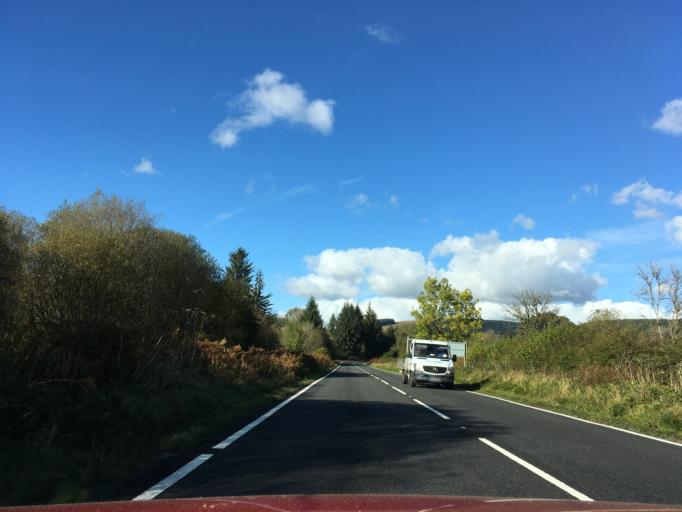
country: GB
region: Wales
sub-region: Merthyr Tydfil County Borough
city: Merthyr Tydfil
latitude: 51.8098
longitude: -3.4434
